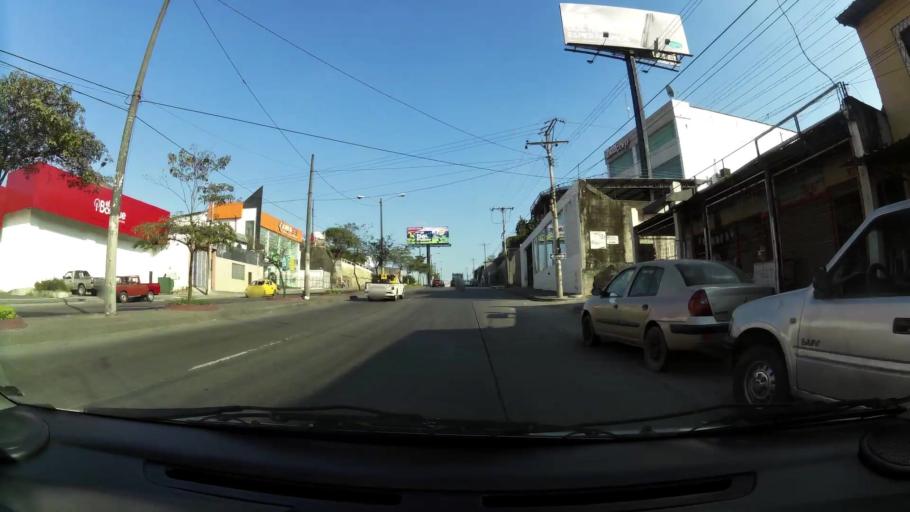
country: EC
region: Guayas
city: Guayaquil
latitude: -2.1544
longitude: -79.9133
